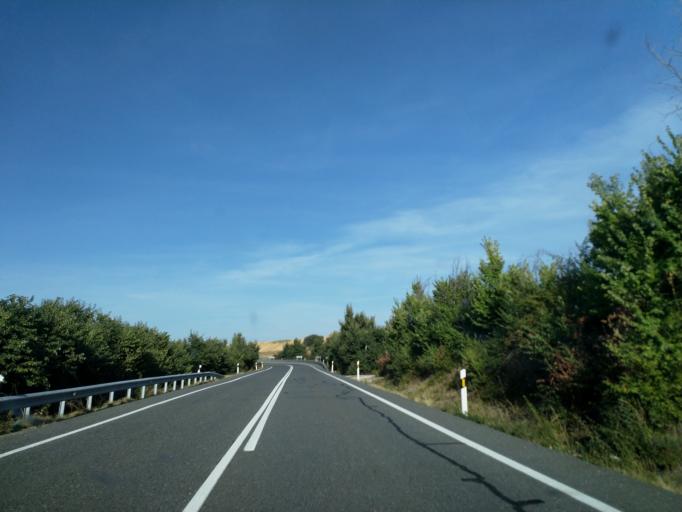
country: ES
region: Castille and Leon
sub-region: Provincia de Segovia
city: Villacastin
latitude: 40.7833
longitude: -4.4085
